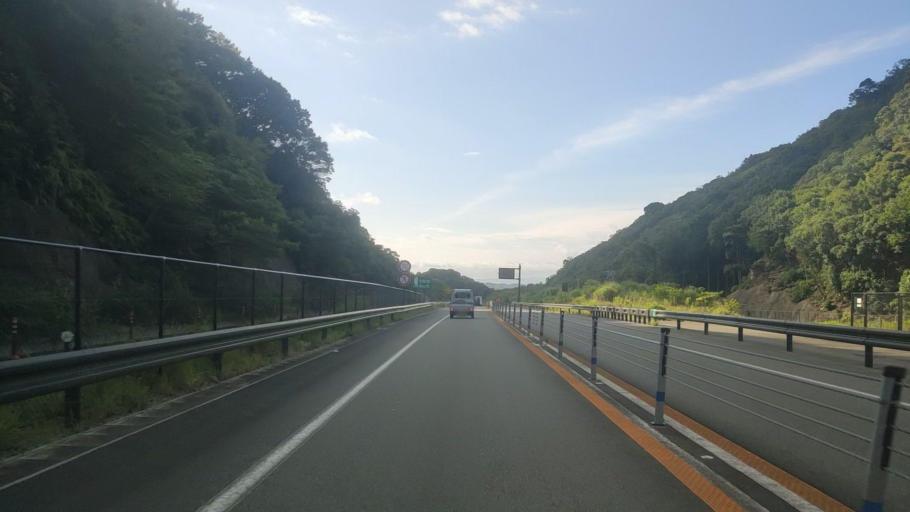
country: JP
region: Wakayama
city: Tanabe
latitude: 33.6331
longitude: 135.4125
